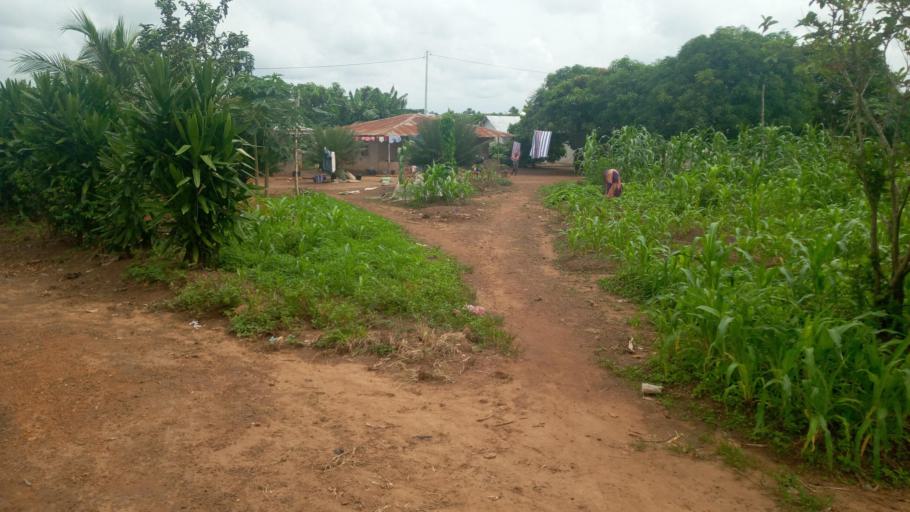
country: SL
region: Southern Province
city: Mogbwemo
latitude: 7.7771
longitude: -12.3015
